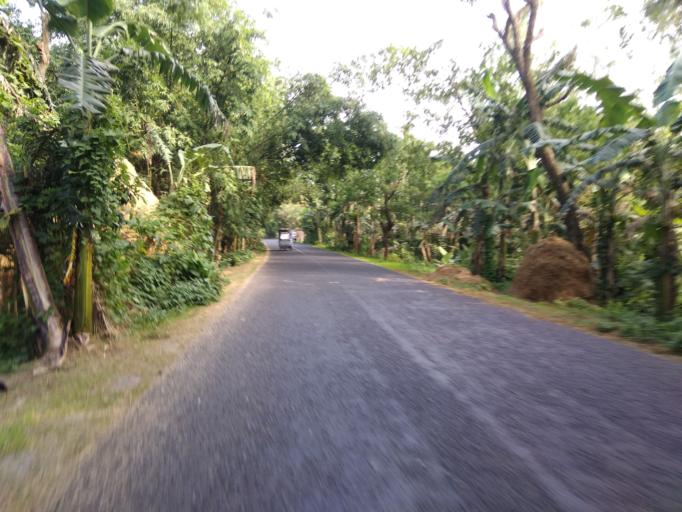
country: BD
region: Rangpur Division
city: Rangpur
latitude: 25.8384
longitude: 89.1141
